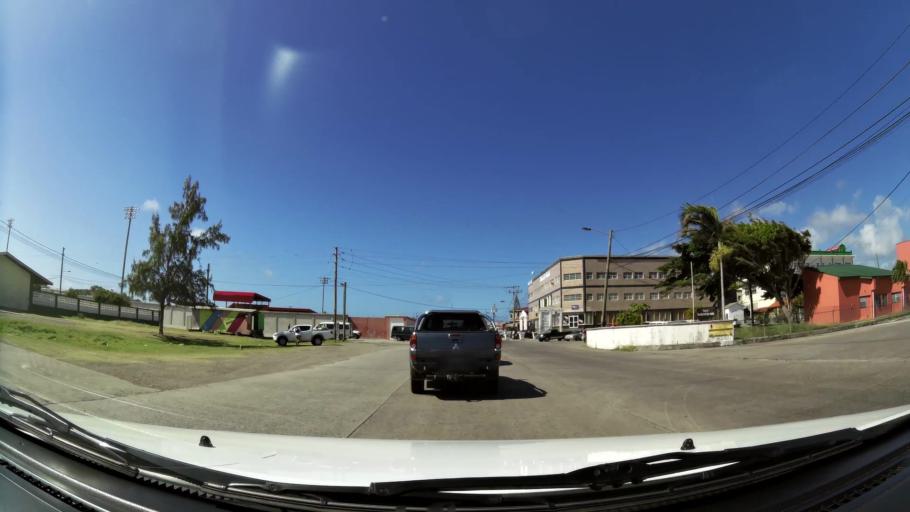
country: LC
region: Vieux-Fort
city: Vieux Fort
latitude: 13.7298
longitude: -60.9499
